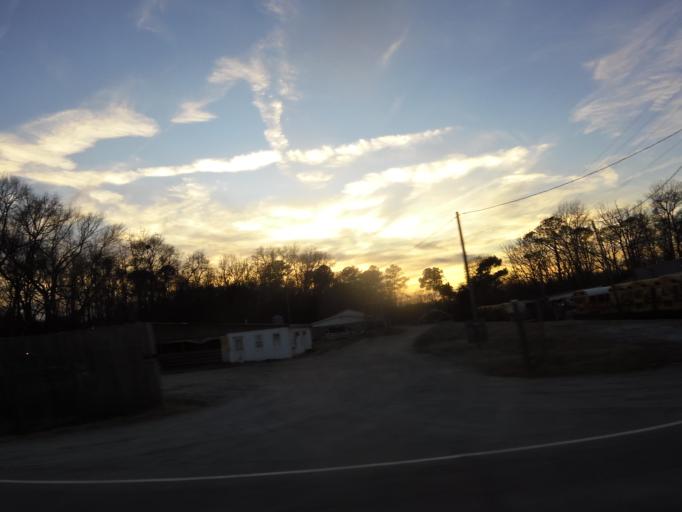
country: US
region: Virginia
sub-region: Southampton County
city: Courtland
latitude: 36.7274
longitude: -77.0722
